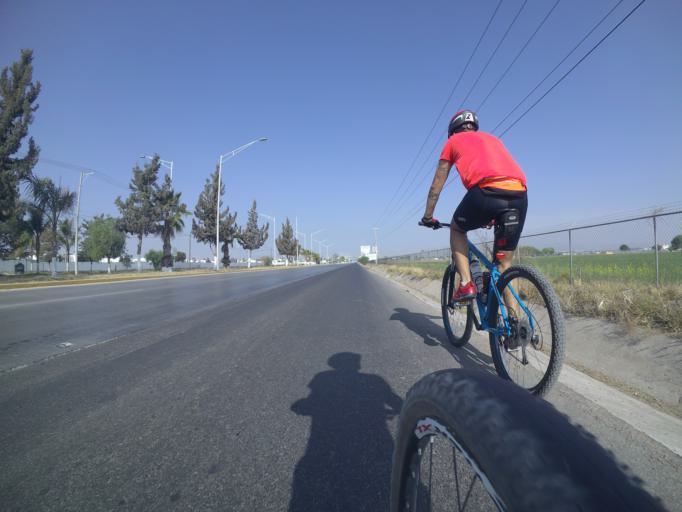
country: MX
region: Aguascalientes
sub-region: Jesus Maria
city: Arboledas Paso Blanco [Fraccionamiento]
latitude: 21.9470
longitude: -102.3026
